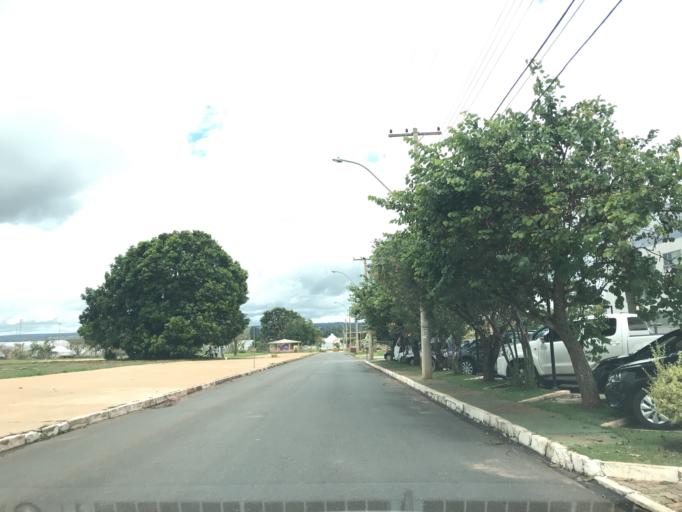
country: BR
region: Federal District
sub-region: Brasilia
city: Brasilia
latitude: -15.7890
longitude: -47.8339
